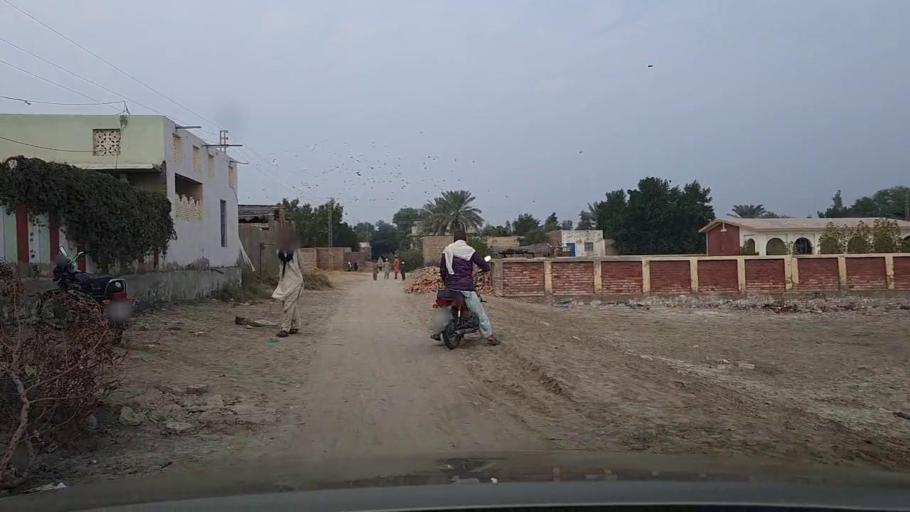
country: PK
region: Sindh
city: Sanghar
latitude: 26.1695
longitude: 68.9571
